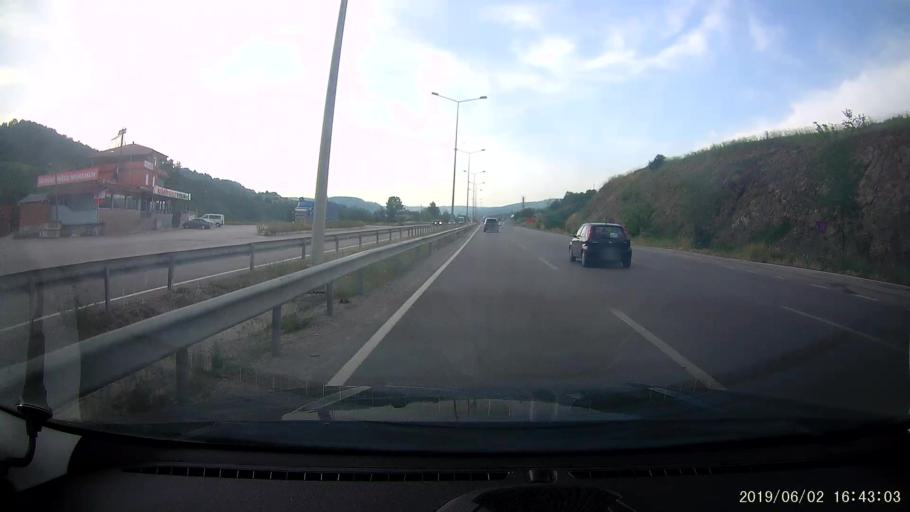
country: TR
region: Samsun
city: Kavak
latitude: 41.1290
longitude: 36.1347
